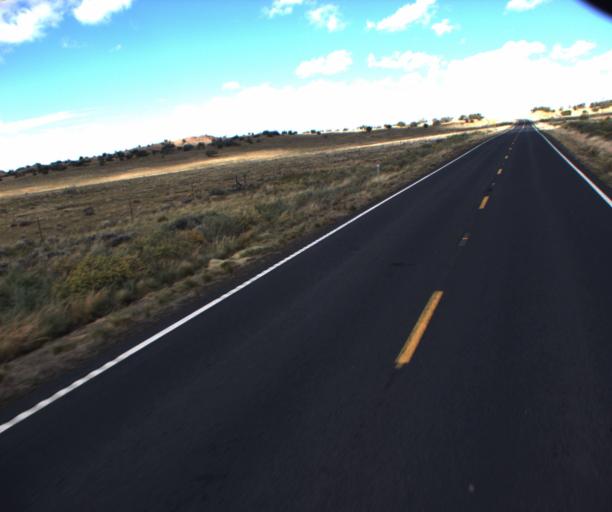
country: US
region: Arizona
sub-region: Apache County
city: Houck
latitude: 35.0658
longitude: -109.2837
